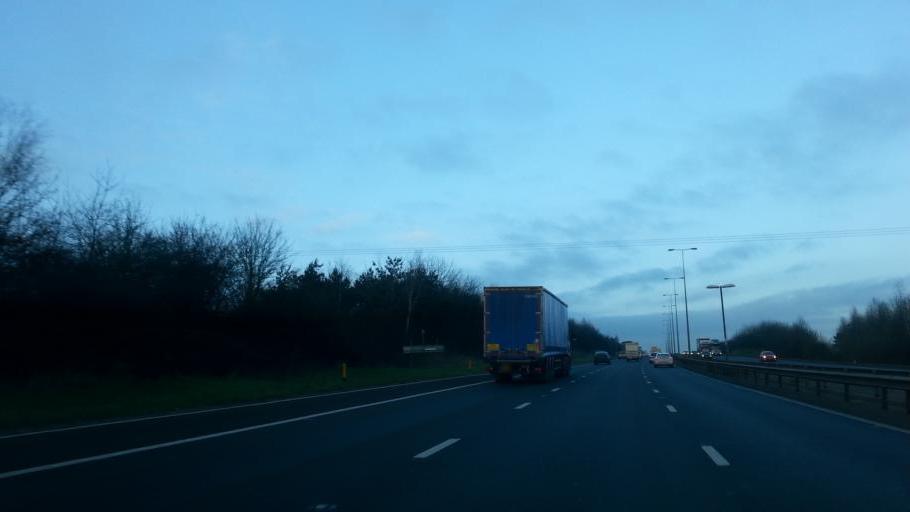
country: GB
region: England
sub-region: Worcestershire
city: Kempsey
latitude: 52.1595
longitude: -2.1885
